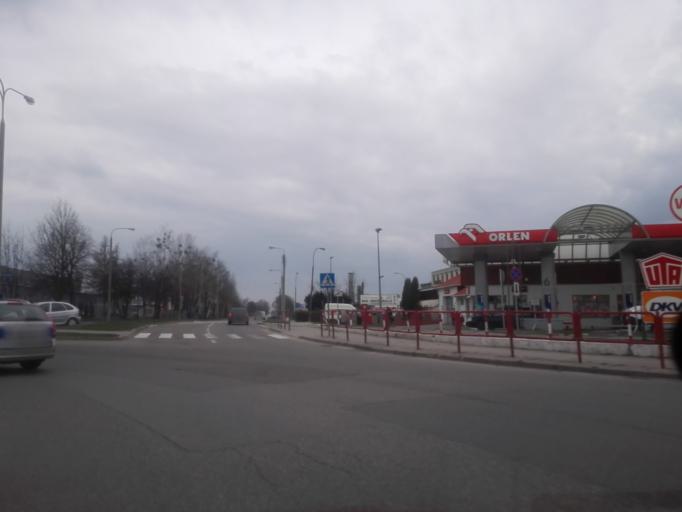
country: PL
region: Podlasie
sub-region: Powiat augustowski
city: Augustow
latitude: 53.8373
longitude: 22.9724
